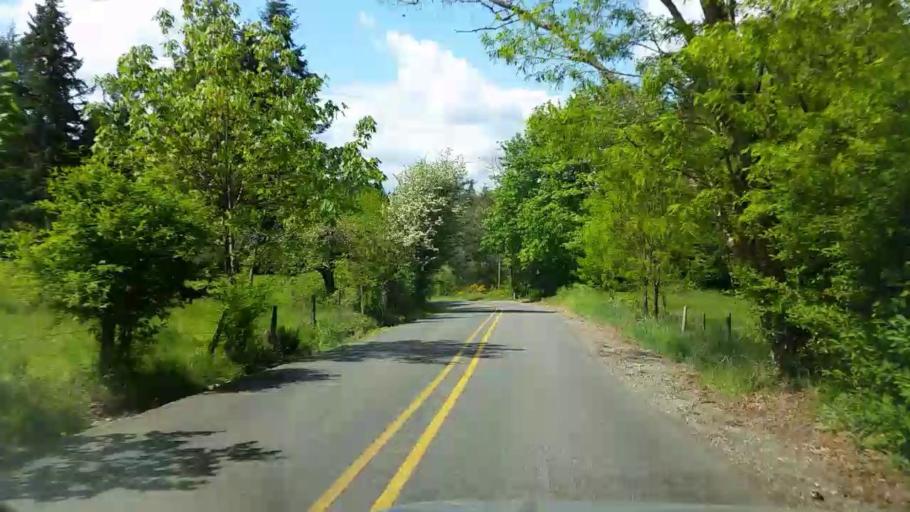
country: US
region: Washington
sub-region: Pierce County
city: Key Center
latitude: 47.3403
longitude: -122.7612
